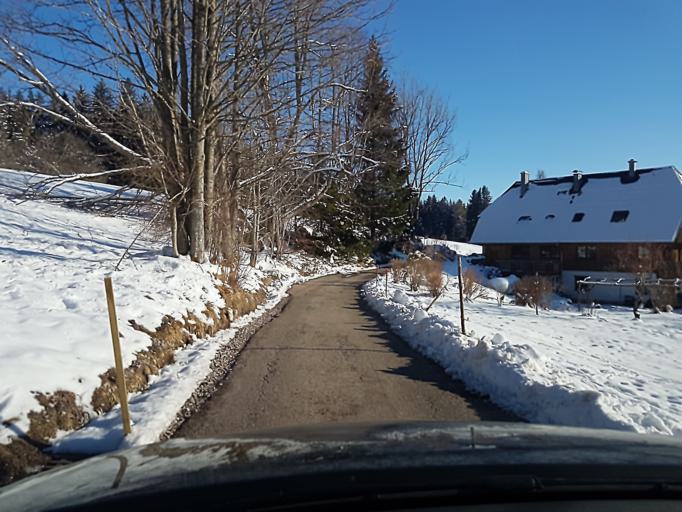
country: DE
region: Baden-Wuerttemberg
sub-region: Freiburg Region
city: Sankt Georgen im Schwarzwald
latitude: 48.1162
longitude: 8.3540
